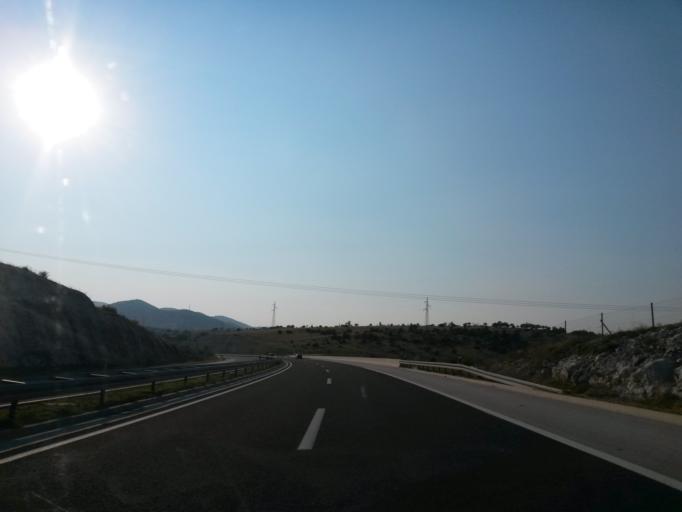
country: HR
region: Splitsko-Dalmatinska
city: Dugopolje
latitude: 43.6015
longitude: 16.6222
